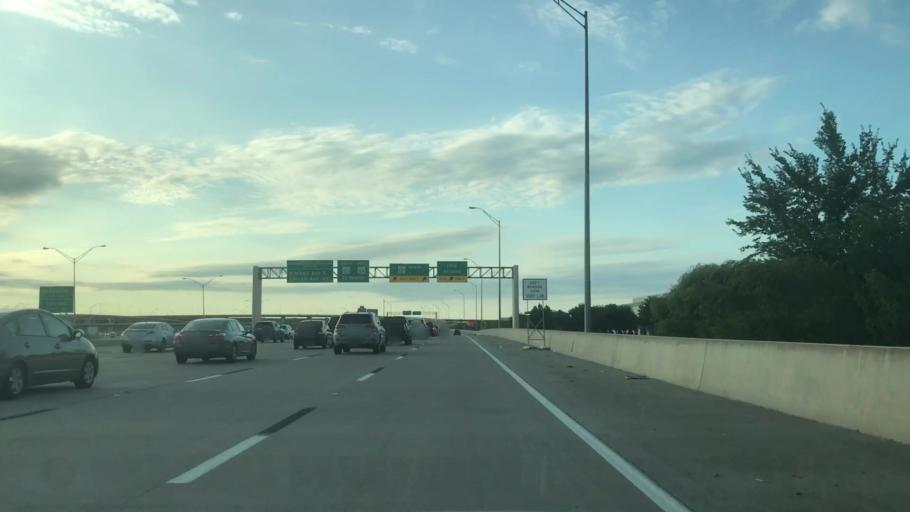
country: US
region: Texas
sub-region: Dallas County
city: Coppell
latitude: 32.9291
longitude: -97.0305
